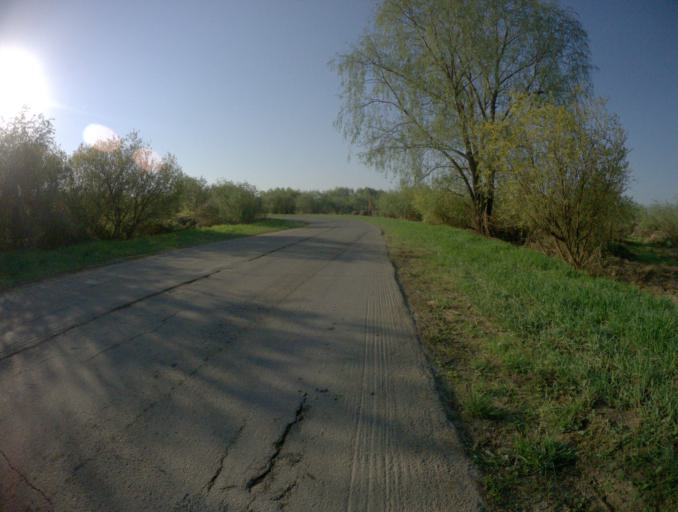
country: RU
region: Vladimir
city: Vyazniki
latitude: 56.2564
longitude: 42.1747
